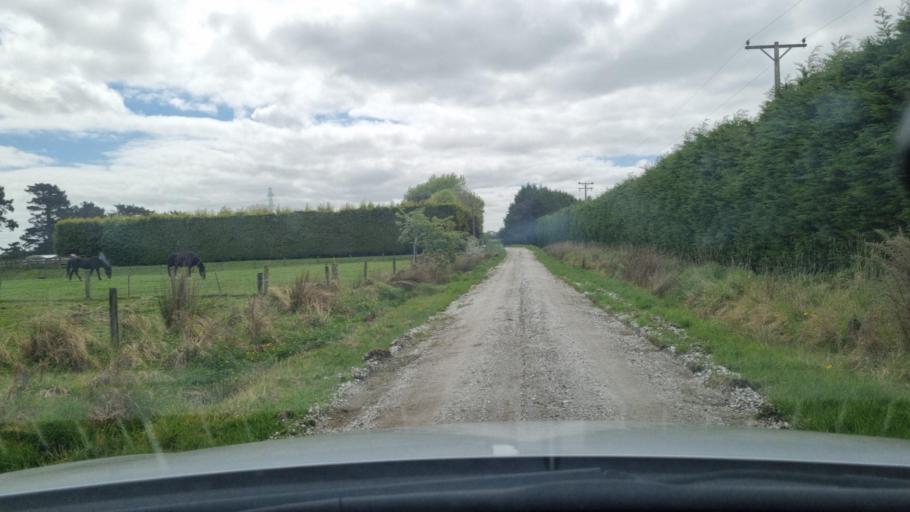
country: NZ
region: Southland
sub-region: Invercargill City
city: Invercargill
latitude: -46.3900
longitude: 168.4046
